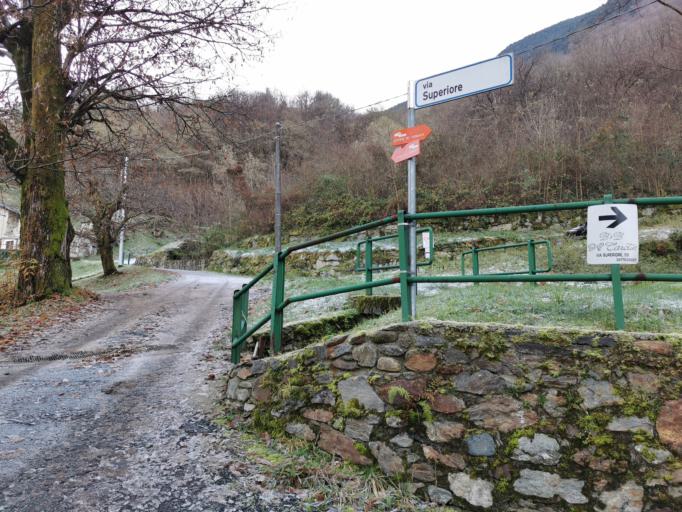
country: IT
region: Lombardy
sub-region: Provincia di Sondrio
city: Andalo Valtellino
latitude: 46.1324
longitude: 9.4769
